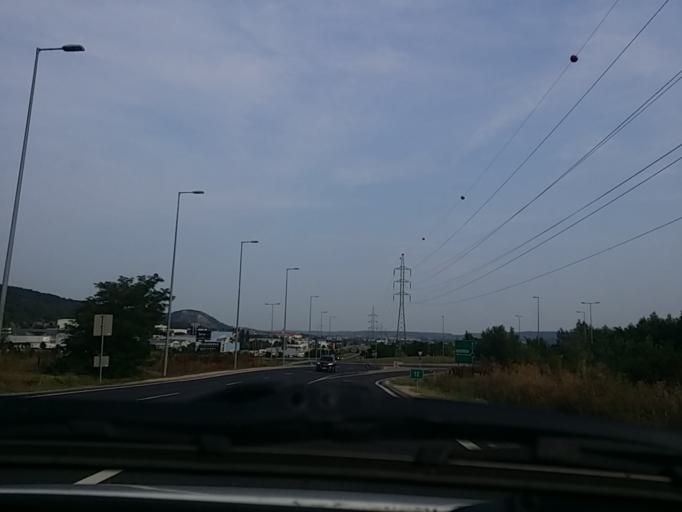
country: HU
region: Pest
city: Biatorbagy
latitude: 47.4733
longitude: 18.8637
